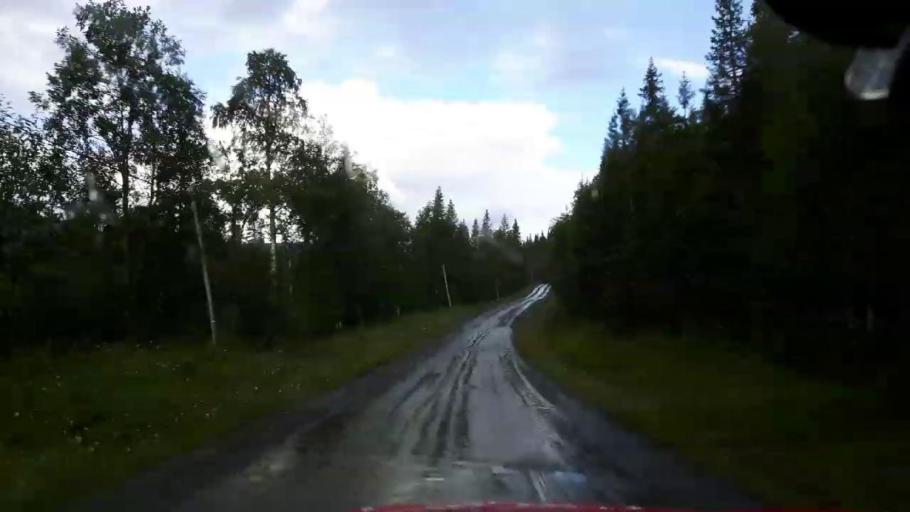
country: NO
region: Nordland
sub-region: Hattfjelldal
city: Hattfjelldal
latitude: 64.8642
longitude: 14.9057
